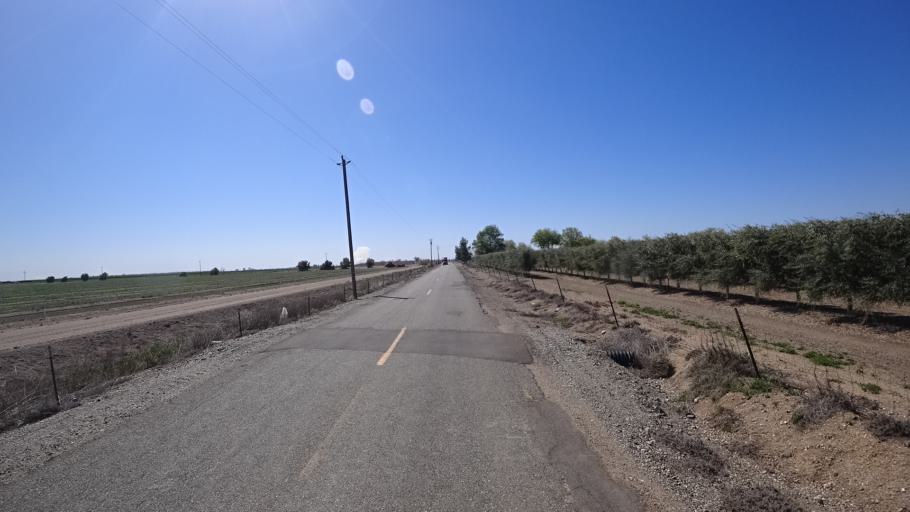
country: US
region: California
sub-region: Glenn County
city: Willows
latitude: 39.6340
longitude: -122.2535
